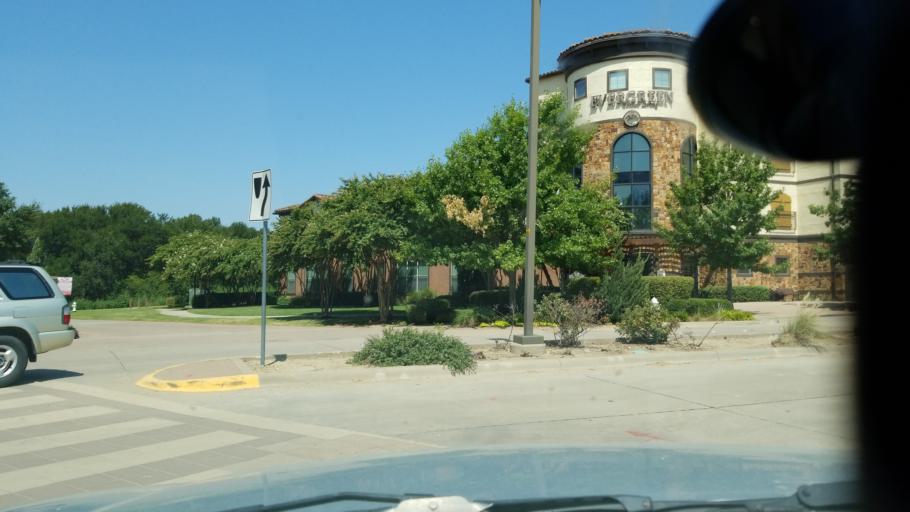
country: US
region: Texas
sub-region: Dallas County
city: Farmers Branch
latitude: 32.9048
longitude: -96.9250
